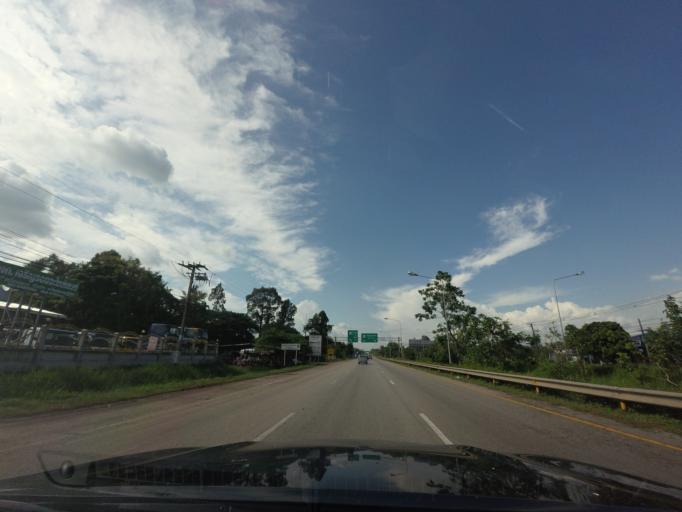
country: TH
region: Nong Khai
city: Sa Khrai
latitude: 17.7646
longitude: 102.7690
